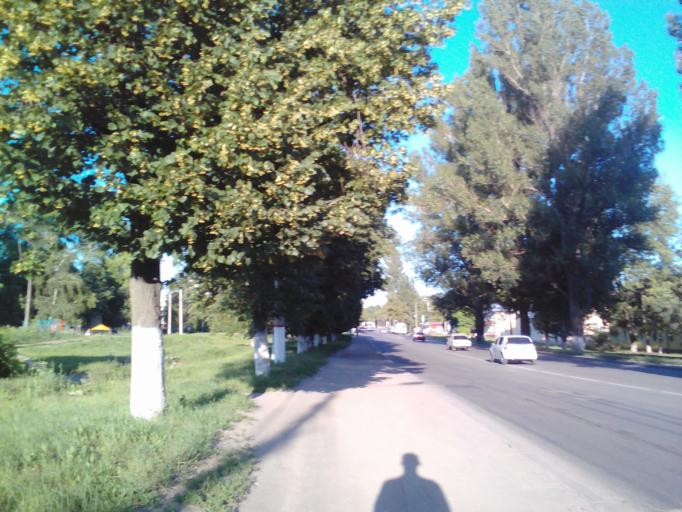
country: RU
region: Kursk
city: Voroshnevo
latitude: 51.6677
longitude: 36.0991
